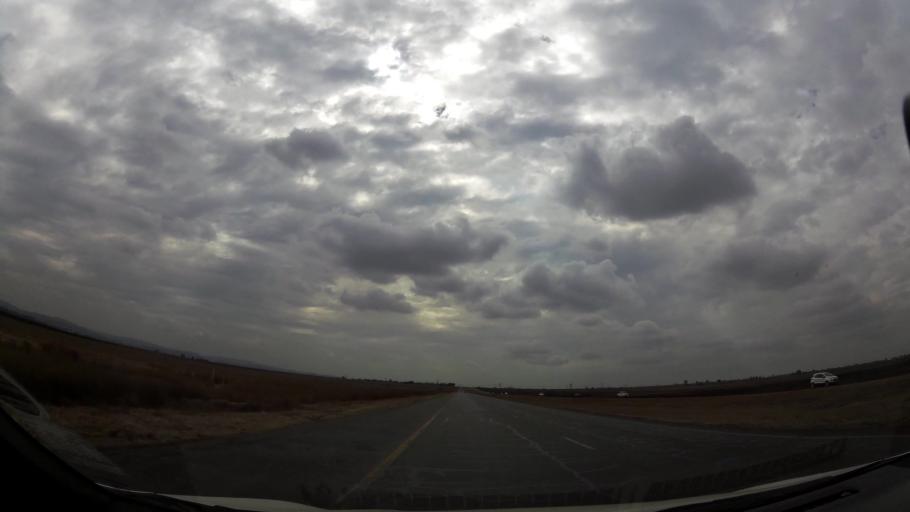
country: ZA
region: Gauteng
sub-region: Ekurhuleni Metropolitan Municipality
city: Germiston
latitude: -26.3747
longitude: 28.0903
